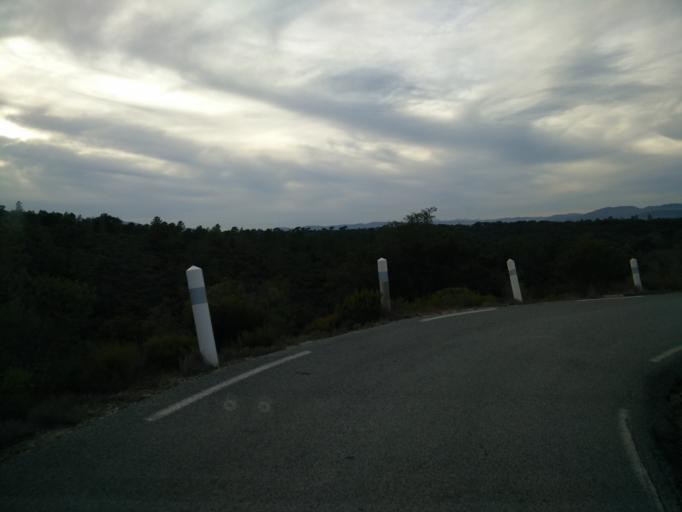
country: FR
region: Provence-Alpes-Cote d'Azur
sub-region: Departement du Var
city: Vidauban
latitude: 43.3850
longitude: 6.4855
